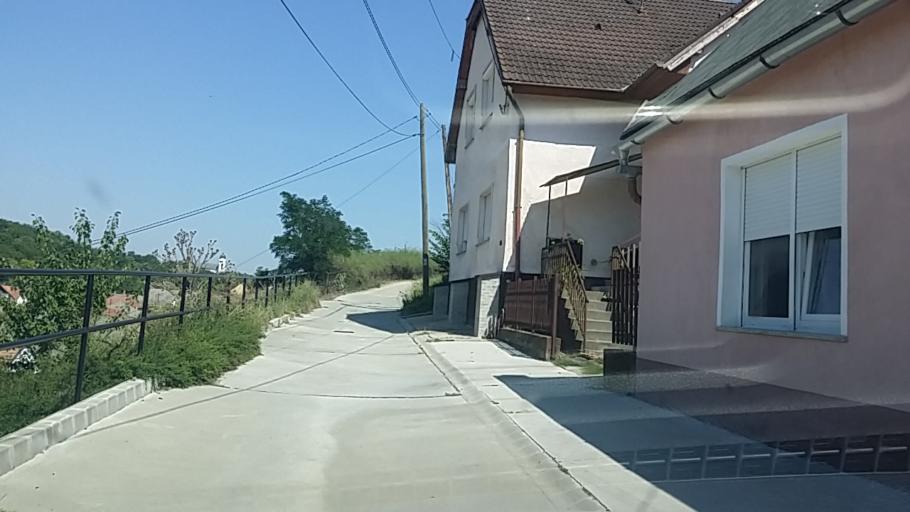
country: HU
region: Tolna
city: Paks
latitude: 46.6563
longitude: 18.8808
